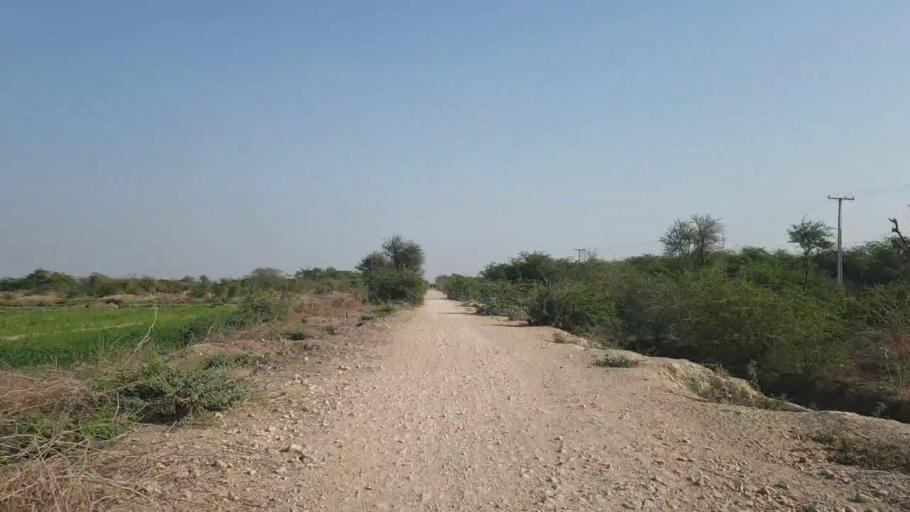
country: PK
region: Sindh
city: Chor
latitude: 25.5164
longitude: 69.6774
